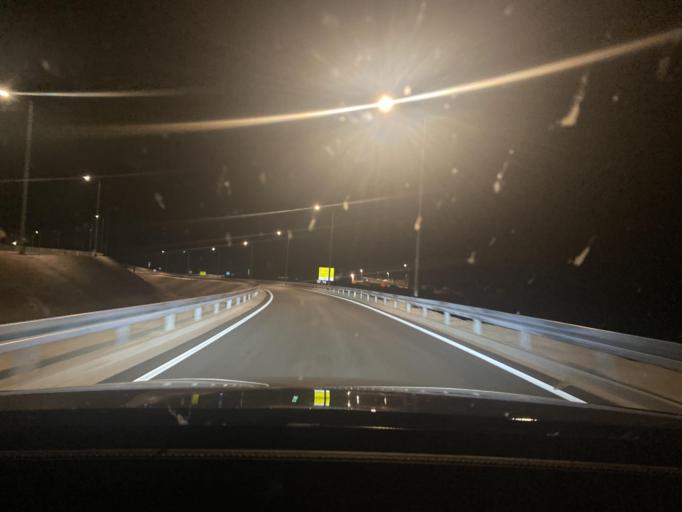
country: BA
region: Federation of Bosnia and Herzegovina
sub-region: Hercegovacko-Bosanski Kanton
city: Neum
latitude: 42.8663
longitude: 17.5642
